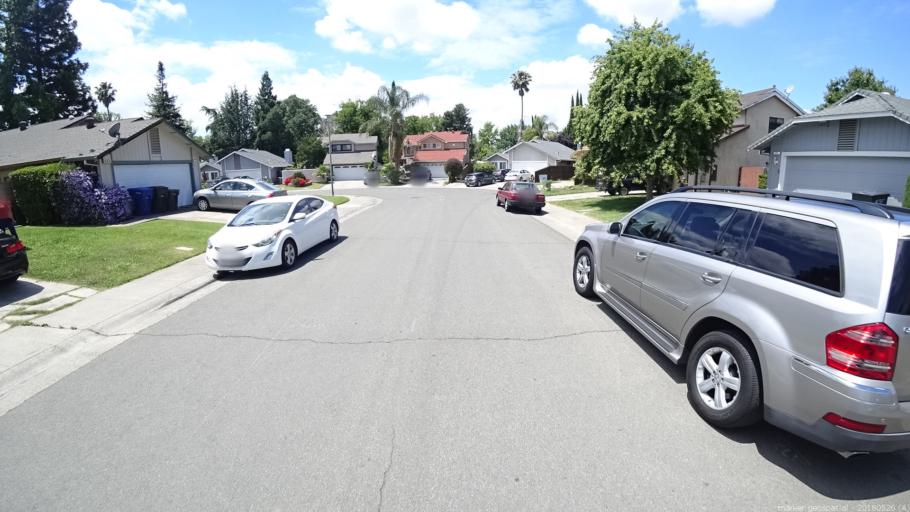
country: US
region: California
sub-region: Sacramento County
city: Sacramento
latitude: 38.6199
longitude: -121.4911
